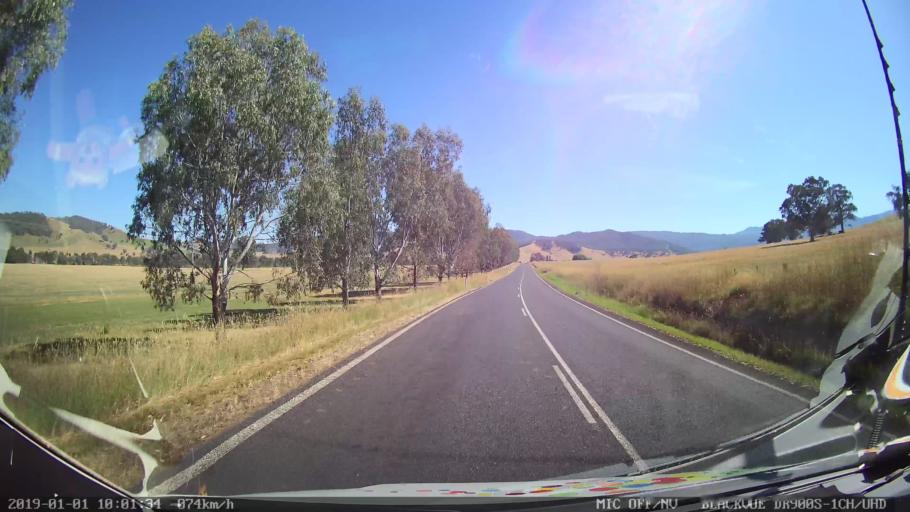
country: AU
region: New South Wales
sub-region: Snowy River
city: Jindabyne
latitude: -36.1902
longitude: 148.1005
